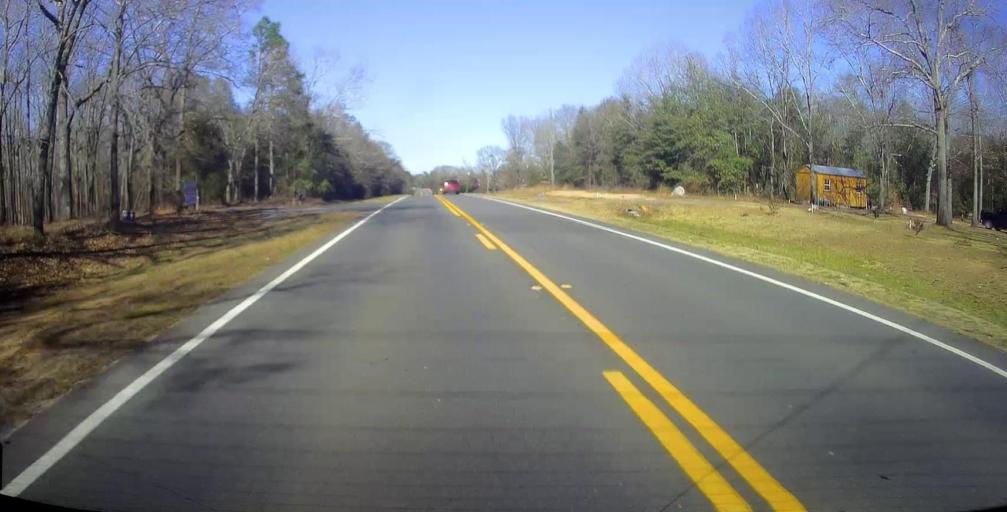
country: US
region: Georgia
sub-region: Macon County
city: Oglethorpe
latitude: 32.2471
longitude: -84.0888
